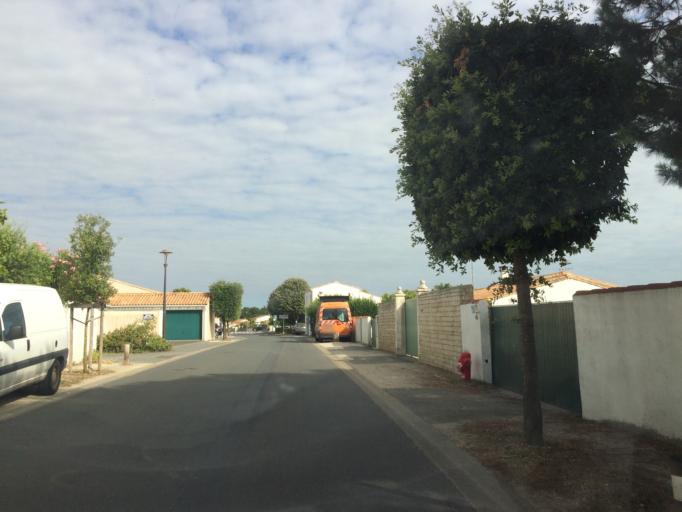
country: FR
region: Poitou-Charentes
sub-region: Departement de la Charente-Maritime
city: La Flotte
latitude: 46.1851
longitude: -1.3312
